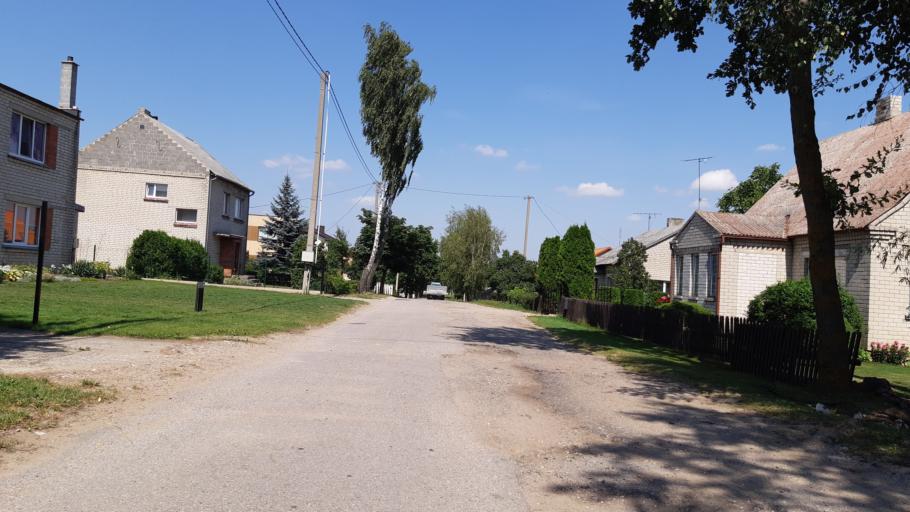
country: LT
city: Virbalis
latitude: 54.6216
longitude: 22.8169
